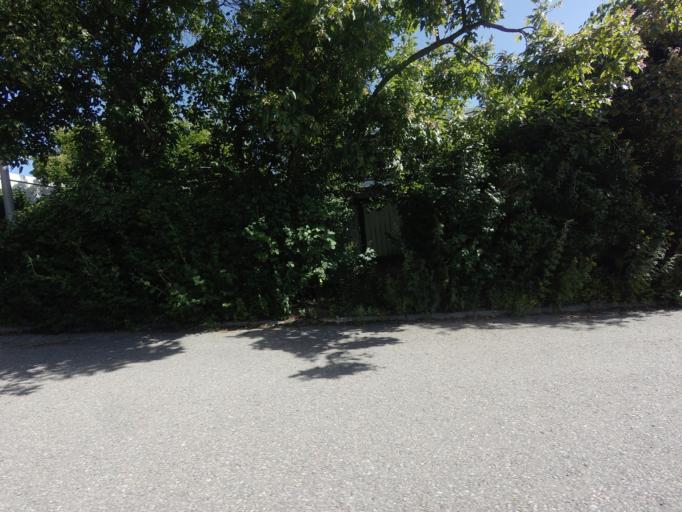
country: FI
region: Uusimaa
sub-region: Helsinki
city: Espoo
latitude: 60.1536
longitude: 24.6310
